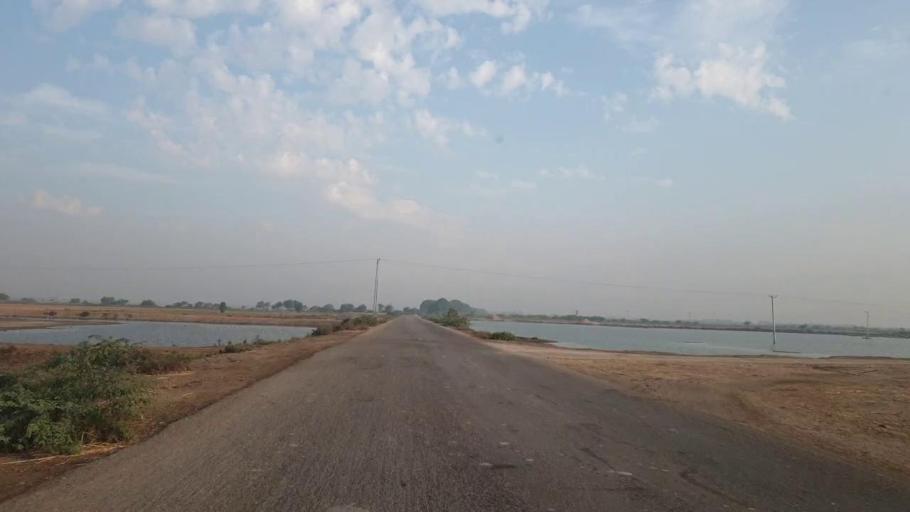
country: PK
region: Sindh
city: Tando Bago
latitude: 24.7218
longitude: 68.9421
